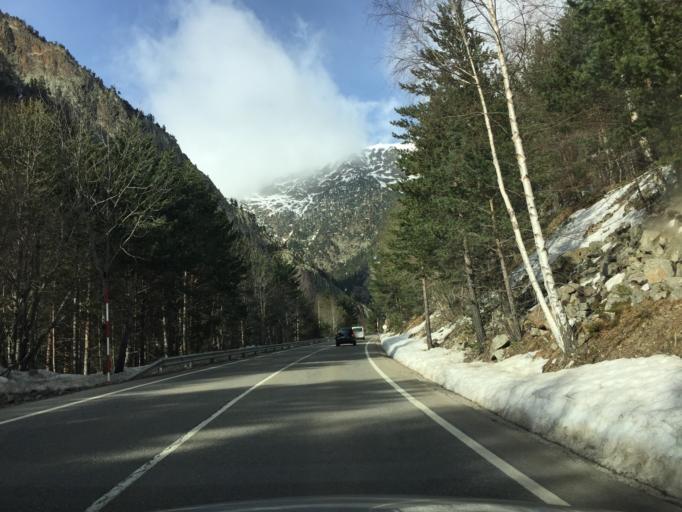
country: ES
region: Aragon
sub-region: Provincia de Huesca
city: Bielsa
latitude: 42.7062
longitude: 0.2016
